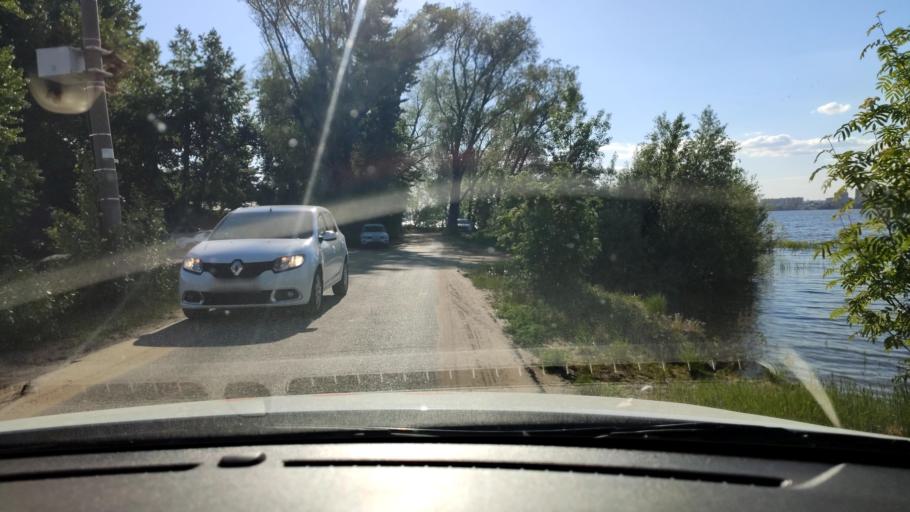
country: RU
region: Tatarstan
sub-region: Gorod Kazan'
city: Kazan
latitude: 55.7878
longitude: 49.0931
